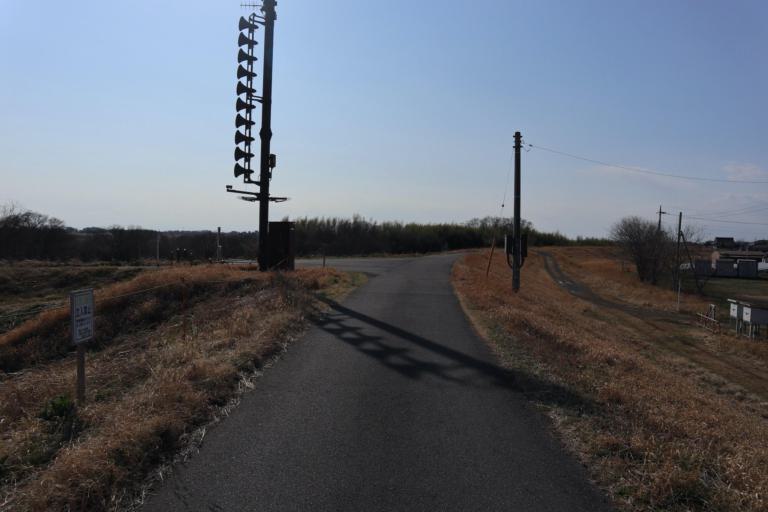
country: JP
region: Tochigi
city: Fujioka
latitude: 36.2608
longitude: 139.6749
